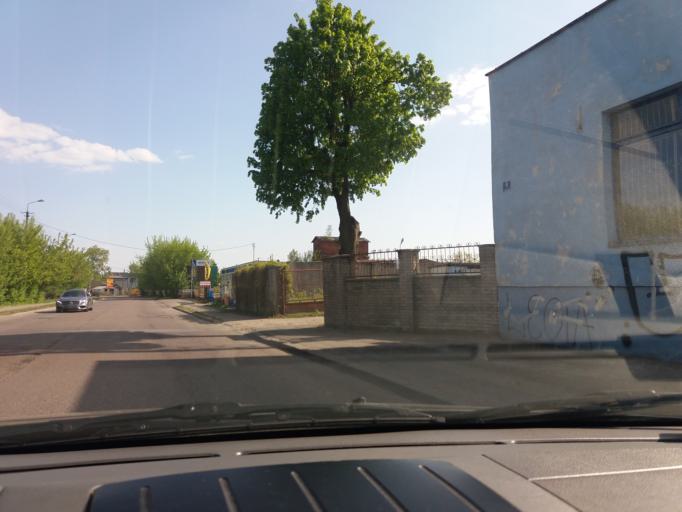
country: PL
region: Masovian Voivodeship
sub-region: Powiat mlawski
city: Mlawa
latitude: 53.1233
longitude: 20.3545
